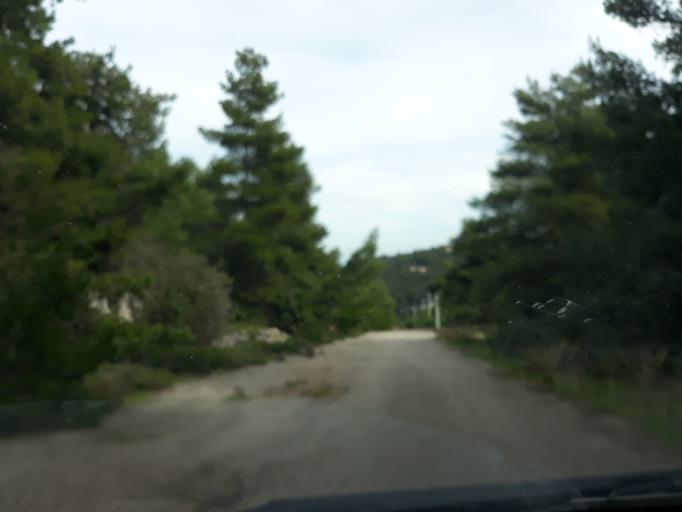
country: GR
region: Attica
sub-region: Nomarchia Anatolikis Attikis
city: Afidnes
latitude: 38.1933
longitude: 23.8002
